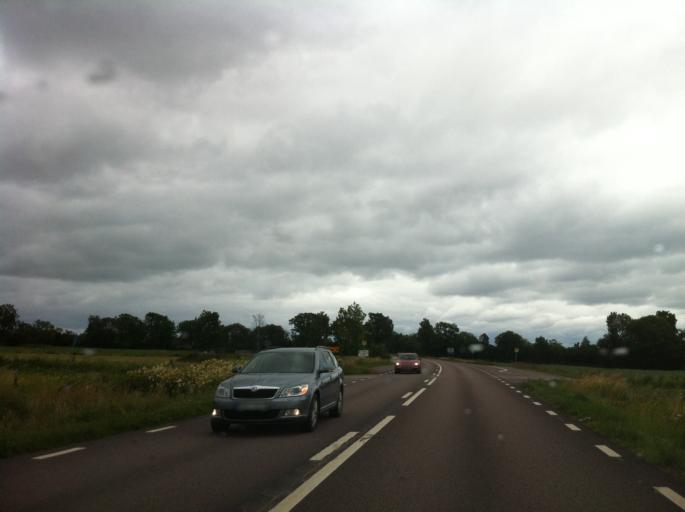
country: SE
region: Kalmar
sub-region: Borgholms Kommun
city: Borgholm
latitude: 57.1421
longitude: 17.0004
